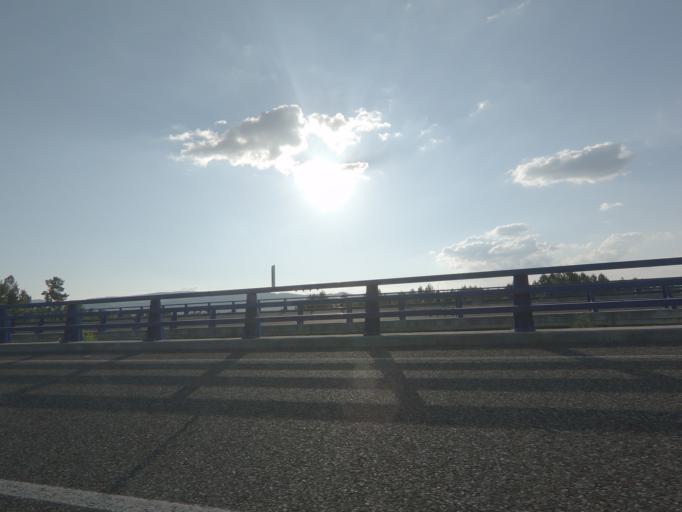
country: ES
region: Galicia
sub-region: Provincia de Ourense
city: Oimbra
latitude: 41.8747
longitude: -7.4318
